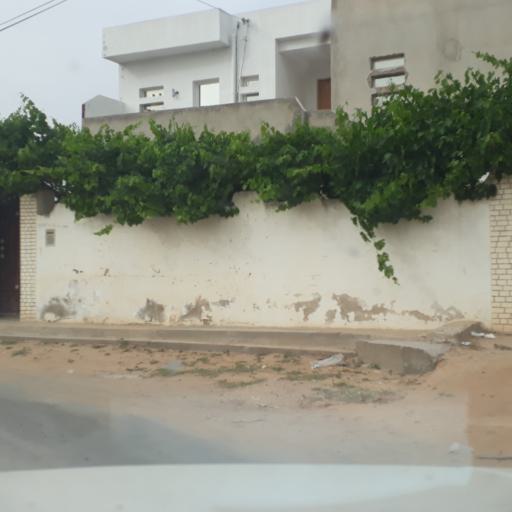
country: TN
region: Safaqis
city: Al Qarmadah
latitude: 34.8229
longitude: 10.7715
